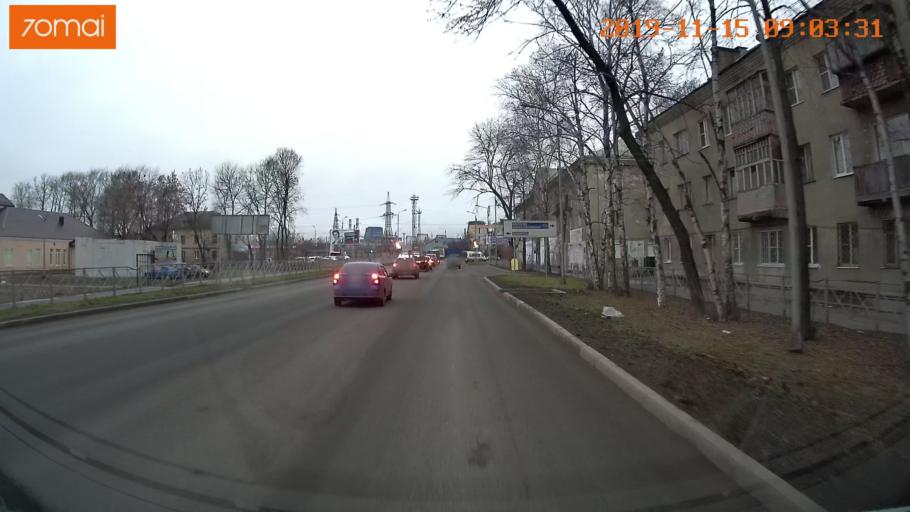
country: RU
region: Vologda
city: Cherepovets
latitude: 59.1389
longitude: 37.9207
